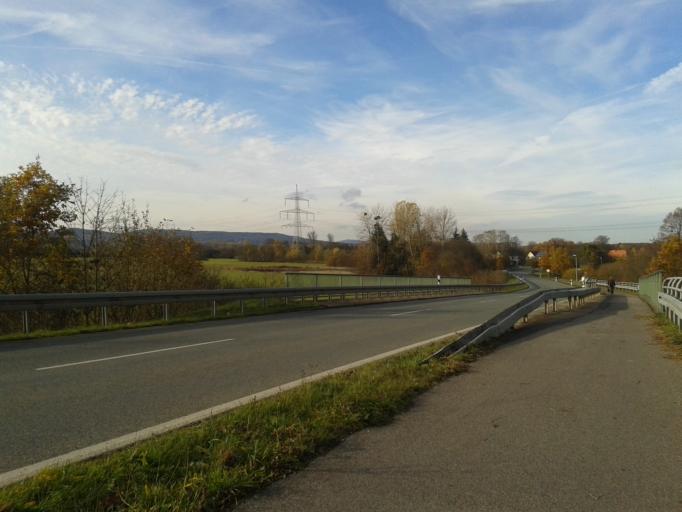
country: DE
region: Bavaria
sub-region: Upper Franconia
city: Gundelsheim
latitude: 49.9312
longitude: 10.9218
